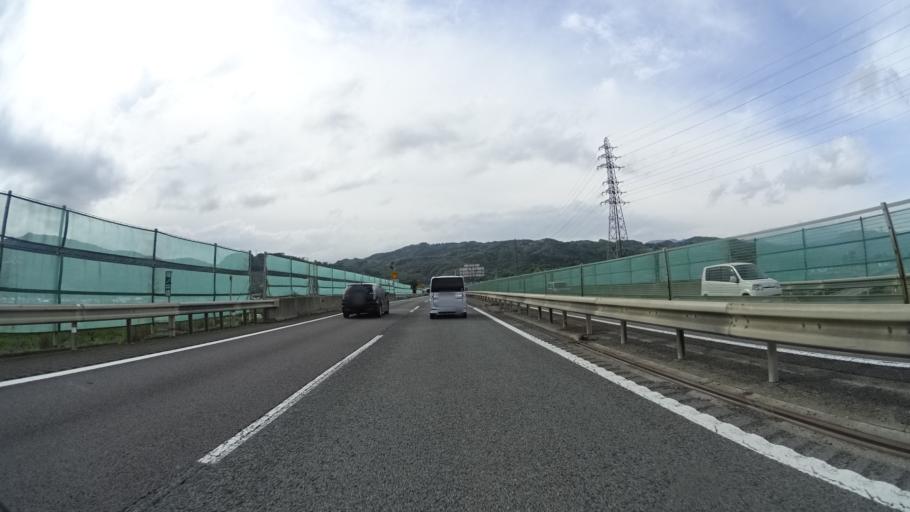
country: JP
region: Nagano
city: Nagano-shi
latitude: 36.5552
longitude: 138.1238
